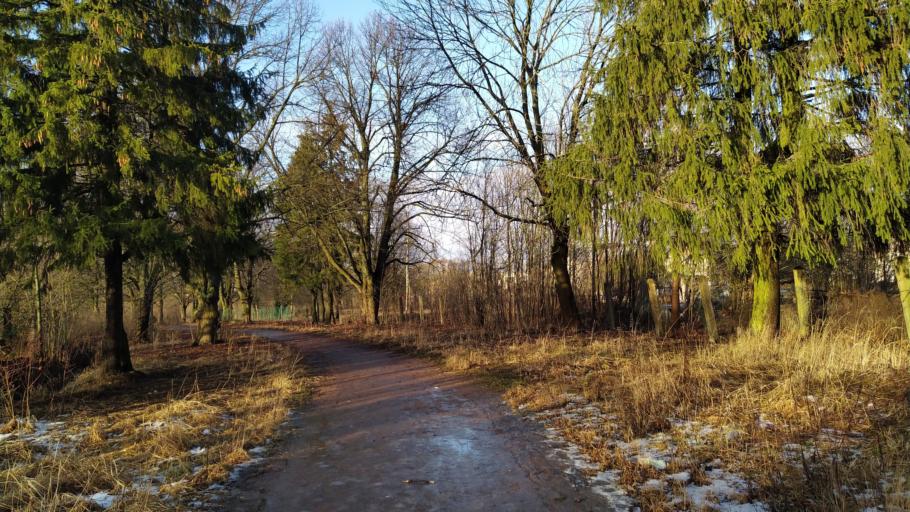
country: RU
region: St.-Petersburg
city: Pushkin
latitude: 59.7272
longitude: 30.3871
